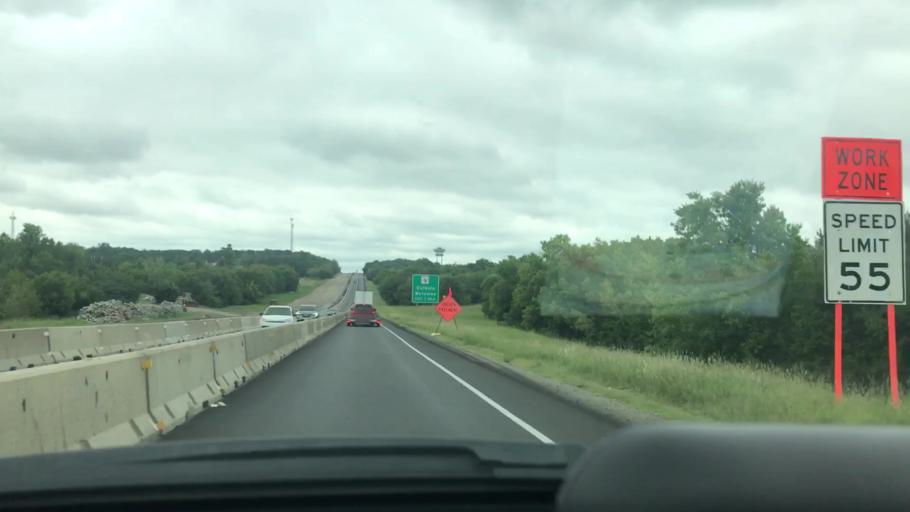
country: US
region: Oklahoma
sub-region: McIntosh County
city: Eufaula
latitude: 35.2773
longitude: -95.5931
